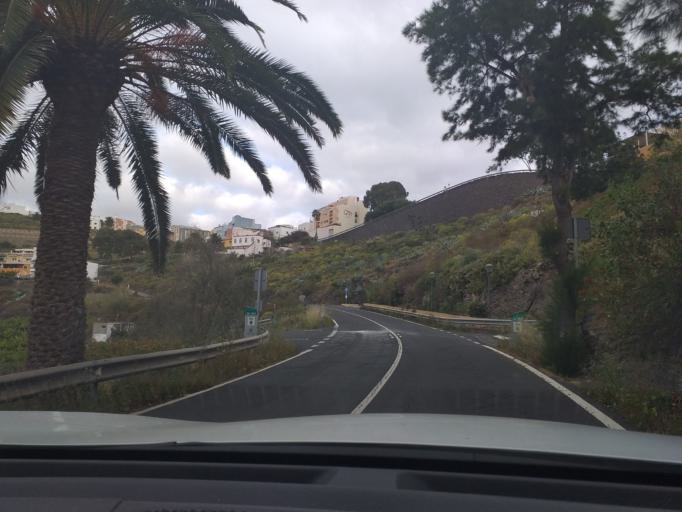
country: ES
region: Canary Islands
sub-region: Provincia de Las Palmas
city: Arucas
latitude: 28.1069
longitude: -15.5027
